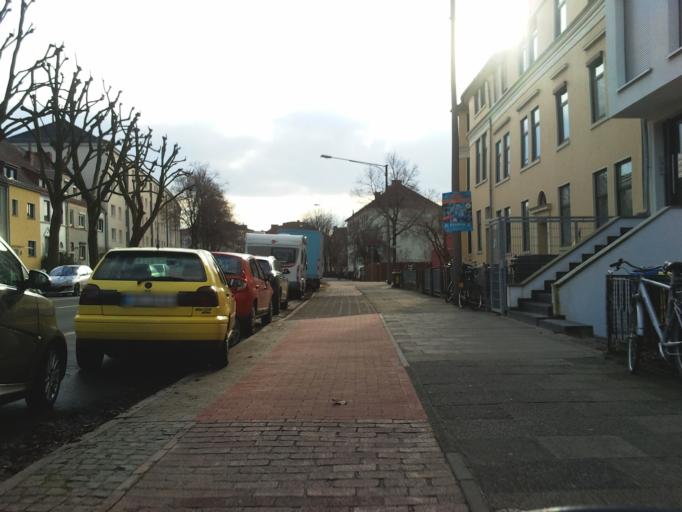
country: DE
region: Bremen
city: Bremen
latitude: 53.0972
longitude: 8.8068
